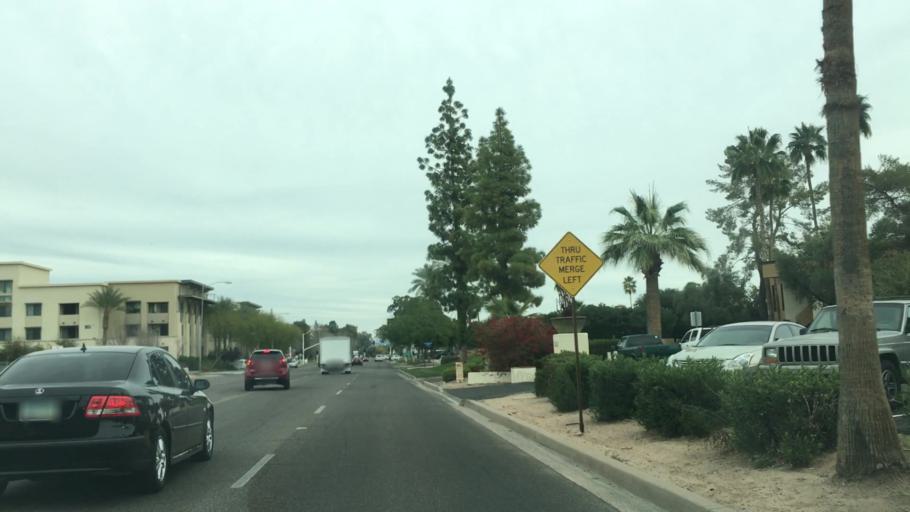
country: US
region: Arizona
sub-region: Maricopa County
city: Paradise Valley
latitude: 33.5313
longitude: -111.9288
